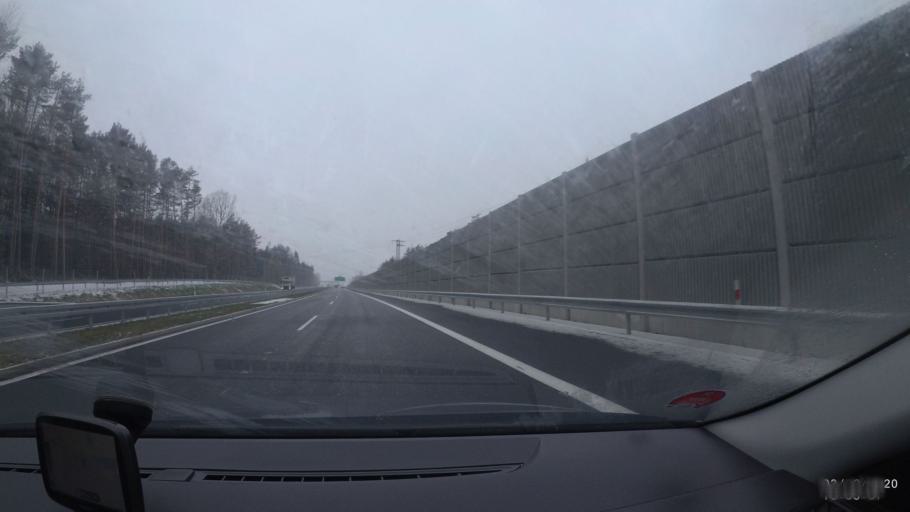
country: CZ
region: Central Bohemia
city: Revnicov
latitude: 50.1740
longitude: 13.8293
